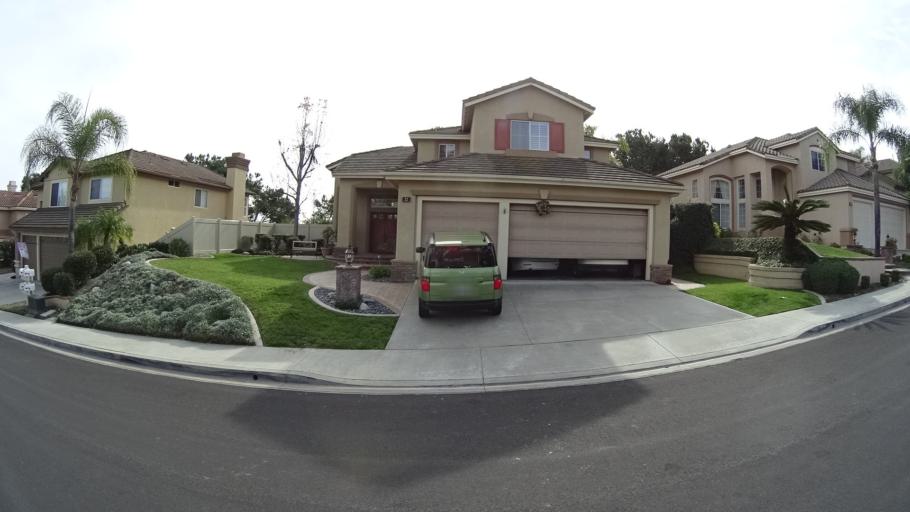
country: US
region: California
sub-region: Orange County
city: Laguna Woods
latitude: 33.5965
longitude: -117.7333
